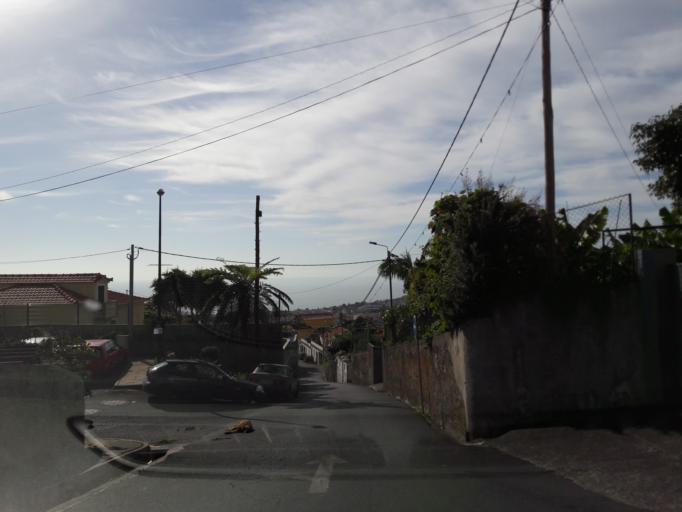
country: PT
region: Madeira
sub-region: Funchal
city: Nossa Senhora do Monte
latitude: 32.6658
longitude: -16.9228
